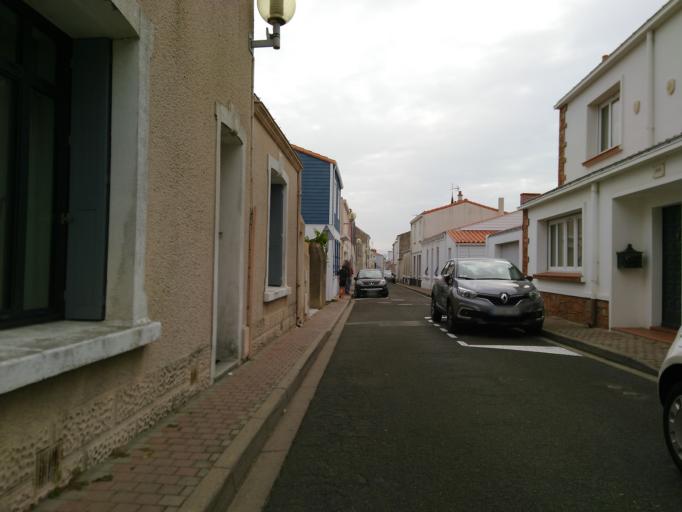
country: FR
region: Pays de la Loire
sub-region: Departement de la Vendee
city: Les Sables-d'Olonne
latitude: 46.4966
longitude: -1.8002
